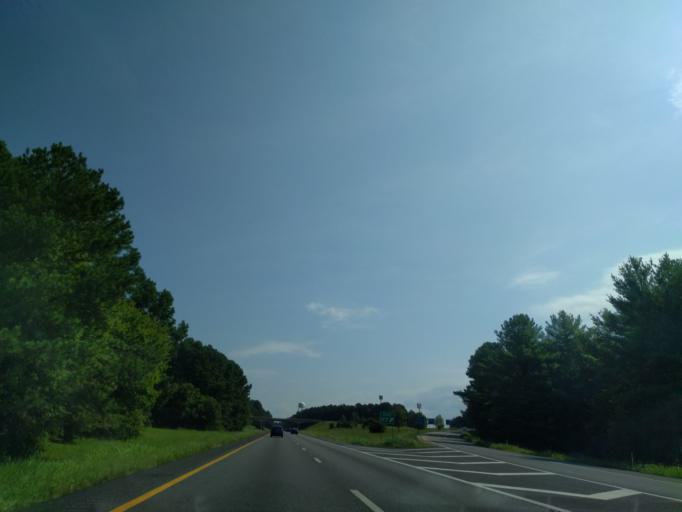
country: US
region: Tennessee
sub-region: Sumner County
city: Portland
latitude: 36.5890
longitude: -86.6030
